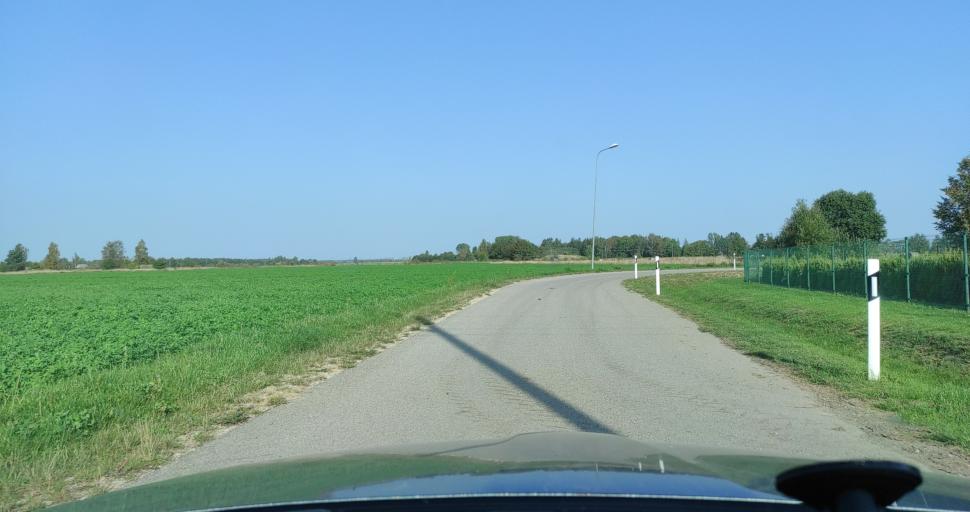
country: LV
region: Ventspils Rajons
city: Piltene
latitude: 57.2296
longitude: 21.6092
